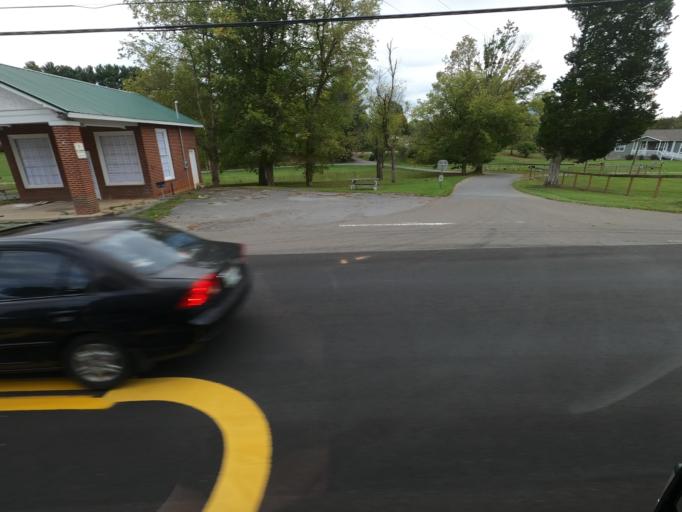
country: US
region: Tennessee
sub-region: Carter County
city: Central
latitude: 36.3268
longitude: -82.2998
